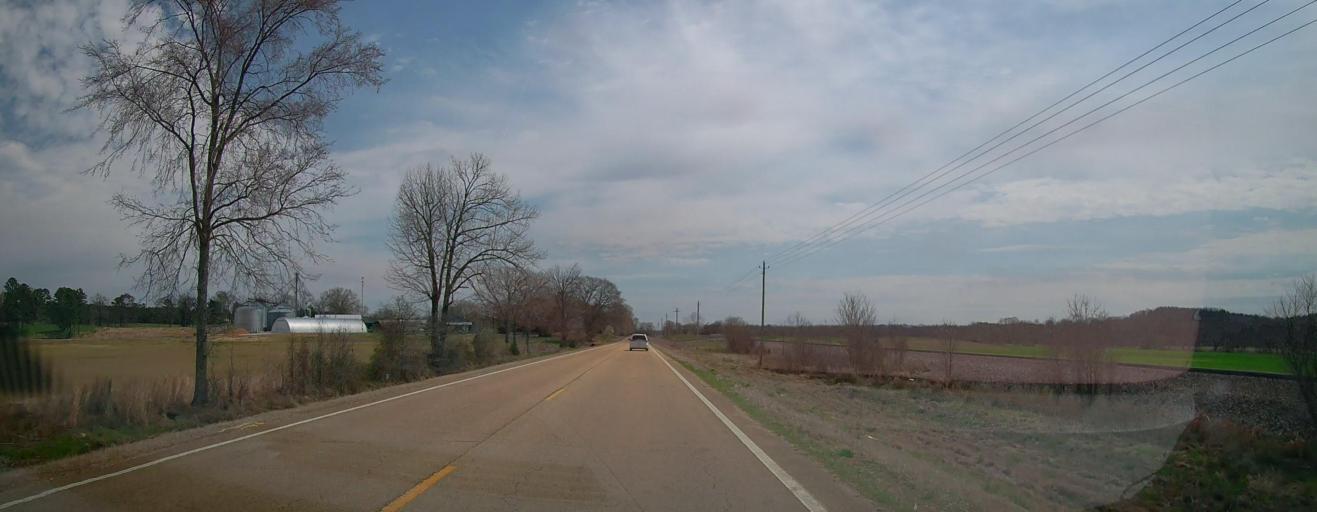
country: US
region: Mississippi
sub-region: Benton County
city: Ashland
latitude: 34.6216
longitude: -89.2349
